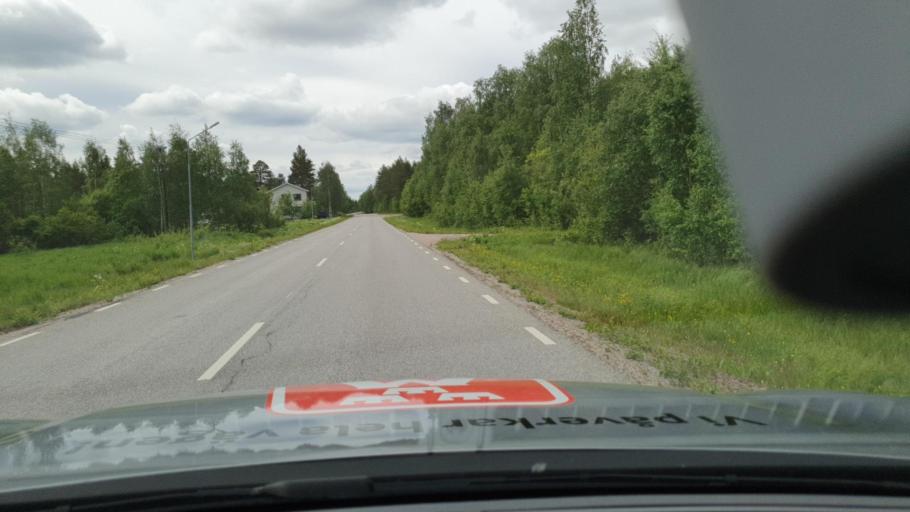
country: FI
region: Lapland
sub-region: Torniolaakso
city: Ylitornio
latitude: 66.0323
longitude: 23.5156
